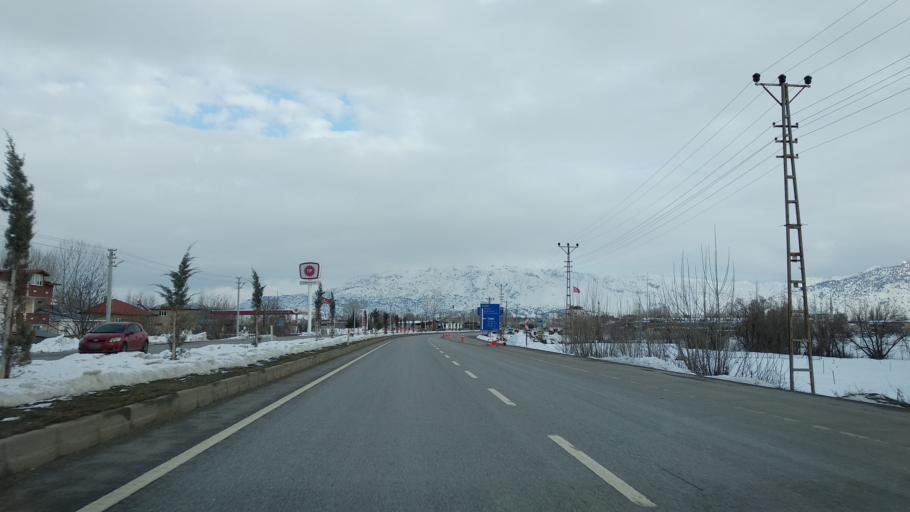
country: TR
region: Kahramanmaras
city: Goksun
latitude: 38.0311
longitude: 36.4759
